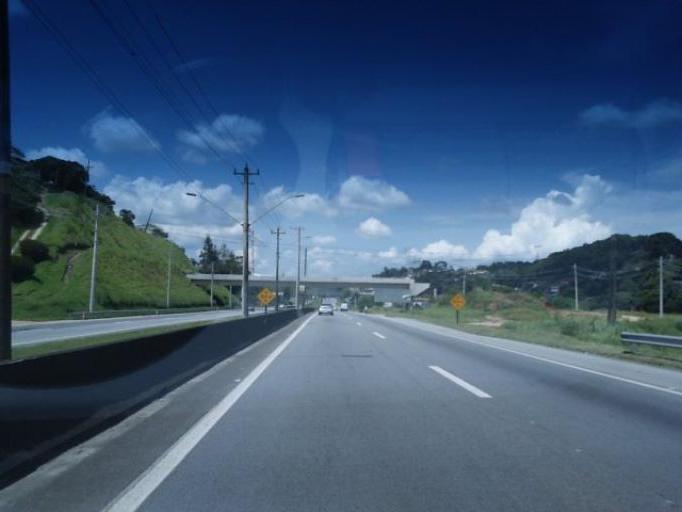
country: BR
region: Sao Paulo
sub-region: Sao Lourenco Da Serra
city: Sao Lourenco da Serra
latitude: -23.8815
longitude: -46.9720
